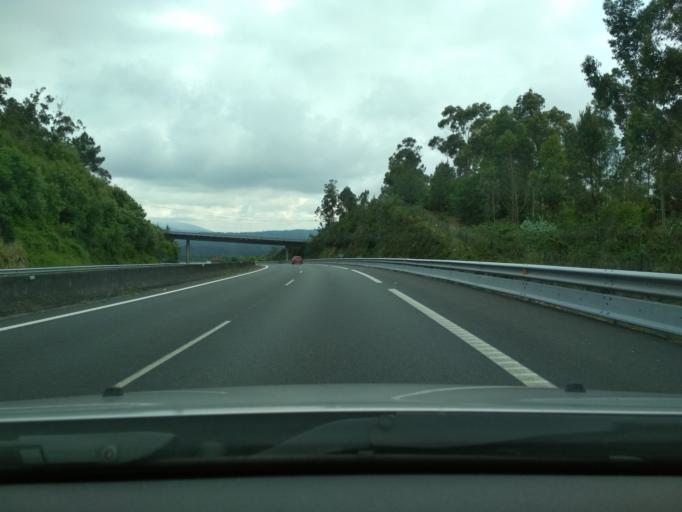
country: ES
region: Galicia
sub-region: Provincia da Coruna
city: Santiago de Compostela
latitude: 42.8369
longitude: -8.5726
